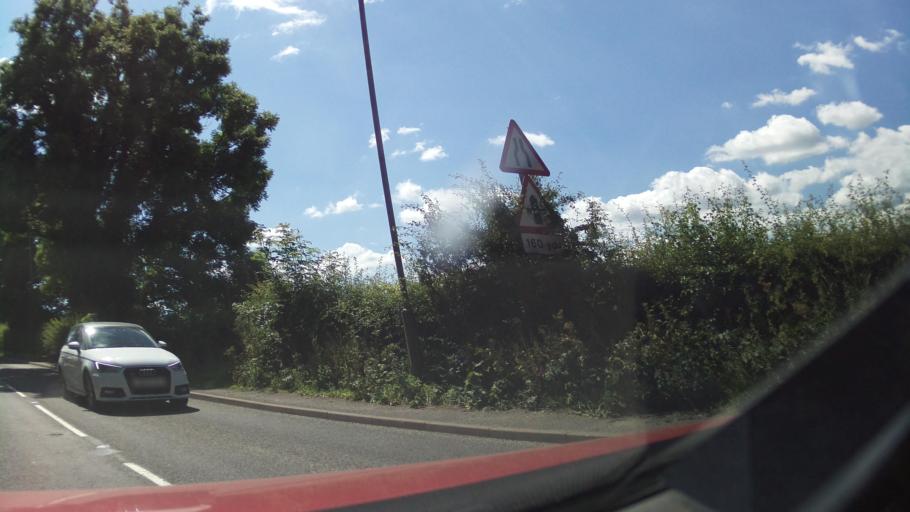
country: GB
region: England
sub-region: Derbyshire
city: Ashbourne
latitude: 53.0223
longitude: -1.7347
